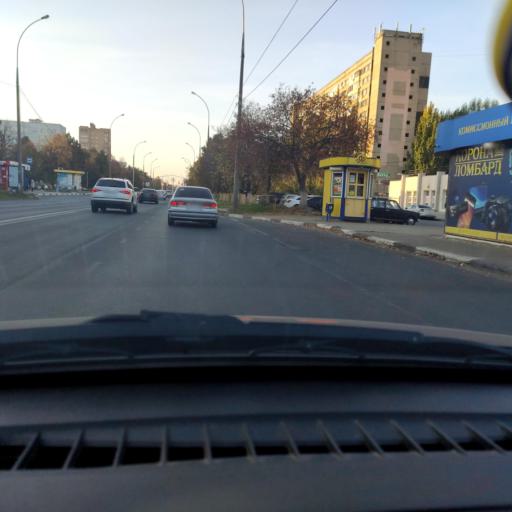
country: RU
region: Samara
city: Tol'yatti
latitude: 53.5293
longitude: 49.3125
